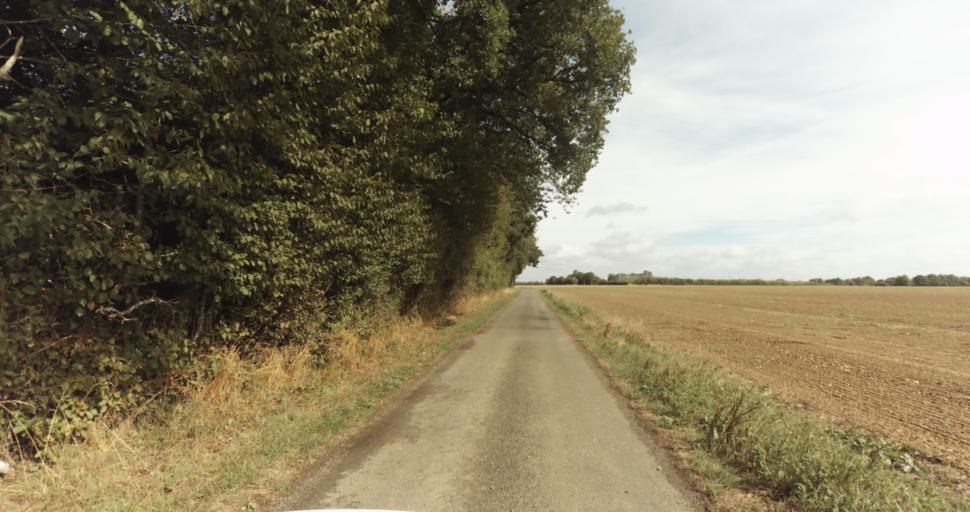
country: FR
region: Lower Normandy
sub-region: Departement de l'Orne
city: Gace
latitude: 48.8315
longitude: 0.3947
